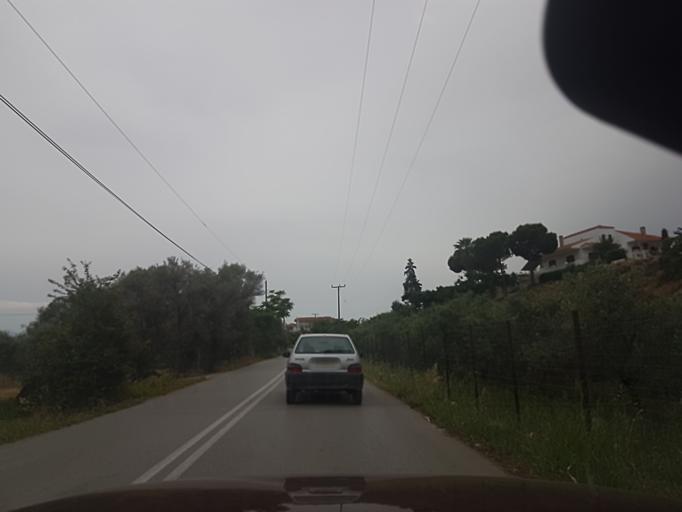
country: GR
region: Central Greece
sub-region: Nomos Evvoias
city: Chalkida
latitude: 38.4655
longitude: 23.6286
